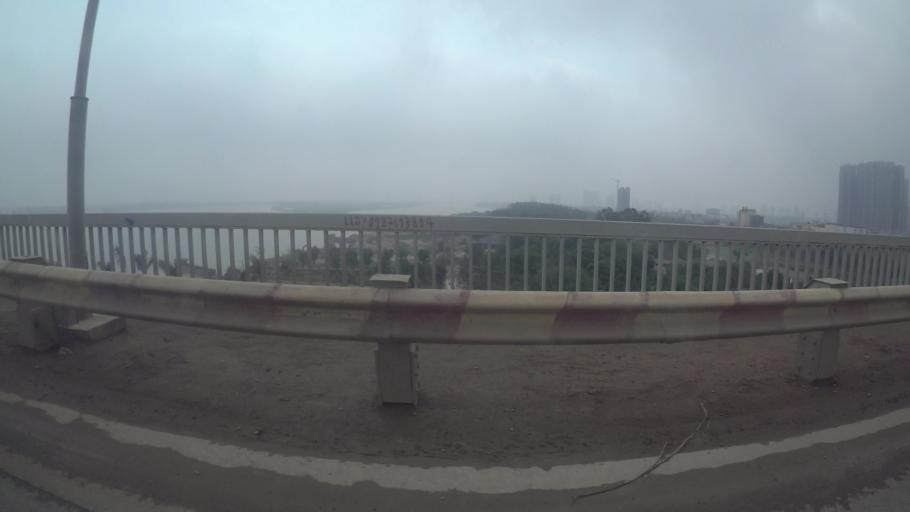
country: VN
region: Ha Noi
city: Tay Ho
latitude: 21.0935
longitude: 105.7862
